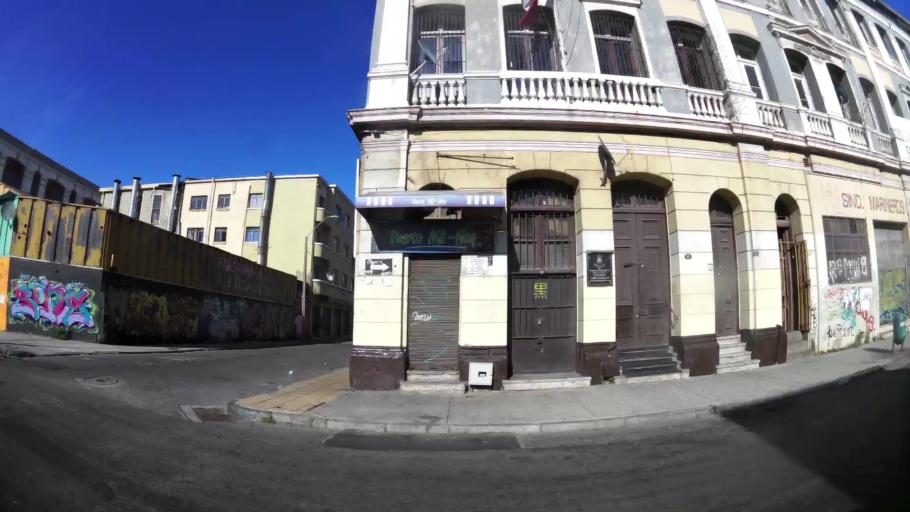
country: CL
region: Valparaiso
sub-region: Provincia de Valparaiso
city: Valparaiso
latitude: -33.0351
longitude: -71.6298
